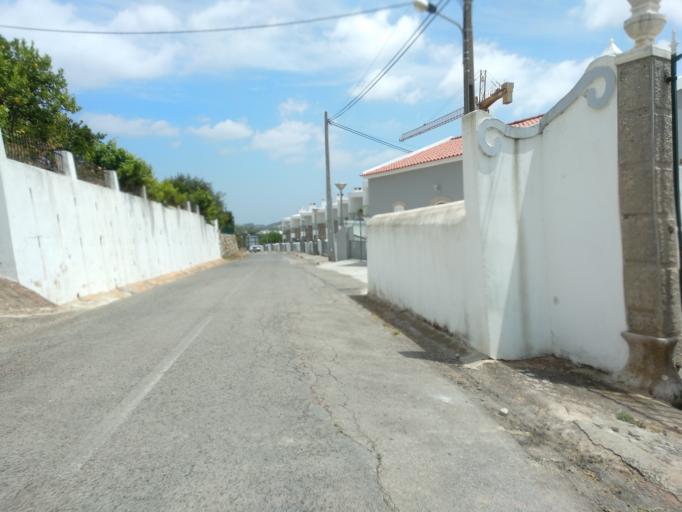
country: PT
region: Faro
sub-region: Sao Bras de Alportel
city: Sao Bras de Alportel
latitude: 37.1623
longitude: -7.8873
